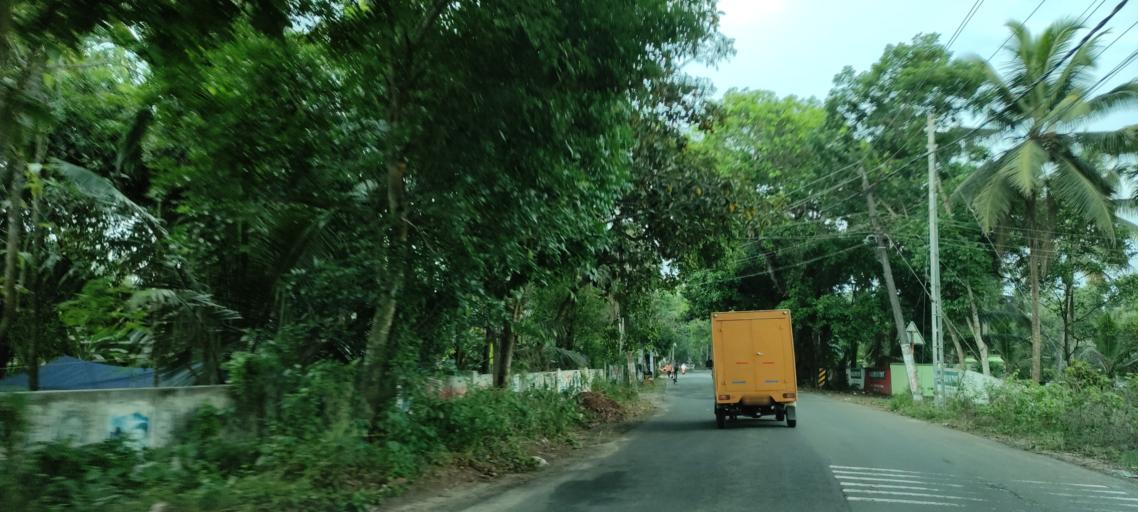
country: IN
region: Kerala
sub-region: Kottayam
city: Vaikam
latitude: 9.7681
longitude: 76.3622
